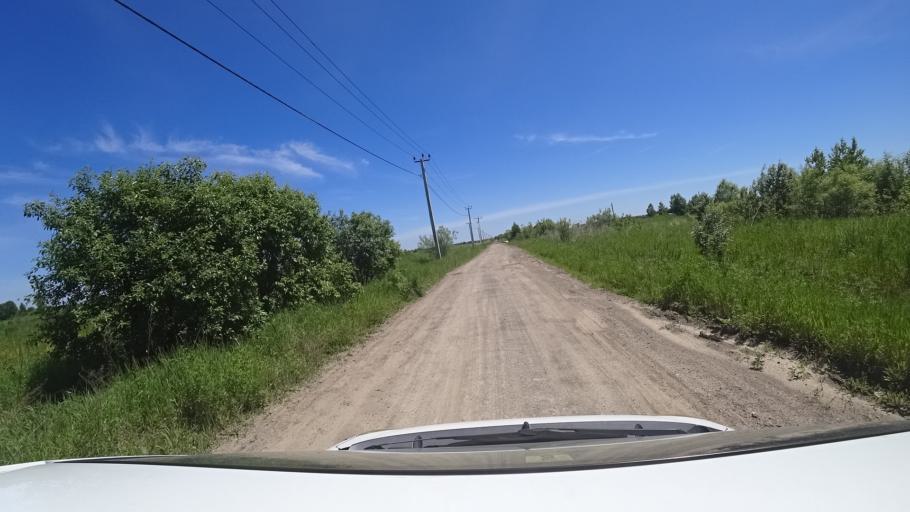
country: RU
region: Khabarovsk Krai
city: Topolevo
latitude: 48.4996
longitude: 135.2018
